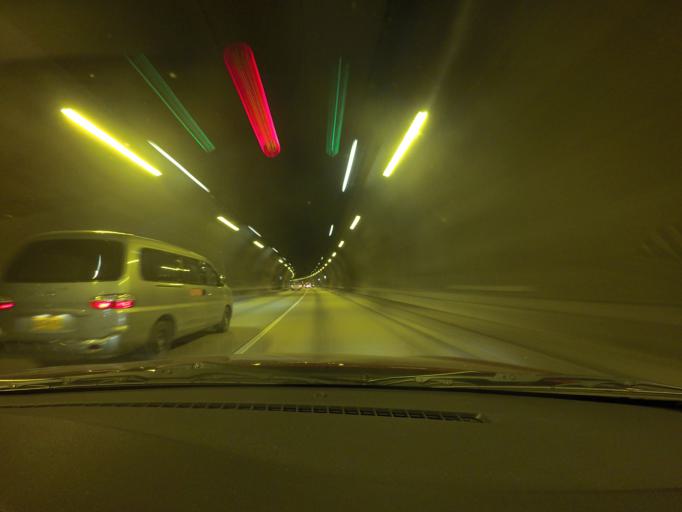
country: CO
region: Cundinamarca
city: Nilo
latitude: 4.2647
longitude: -74.5800
